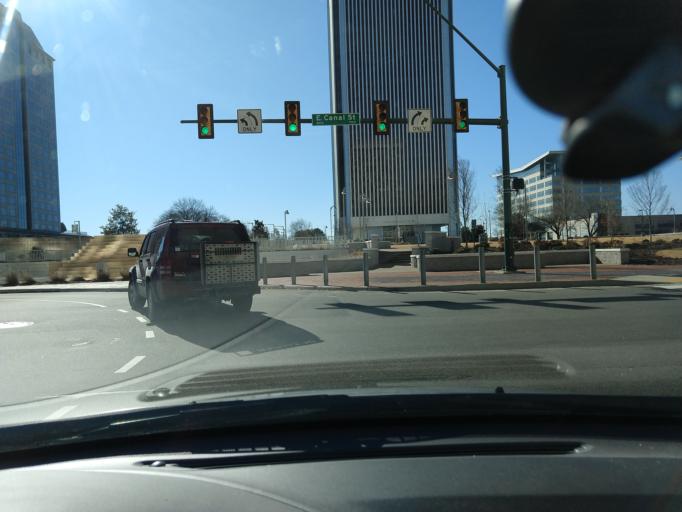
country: US
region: Virginia
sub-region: City of Richmond
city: Richmond
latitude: 37.5370
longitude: -77.4388
